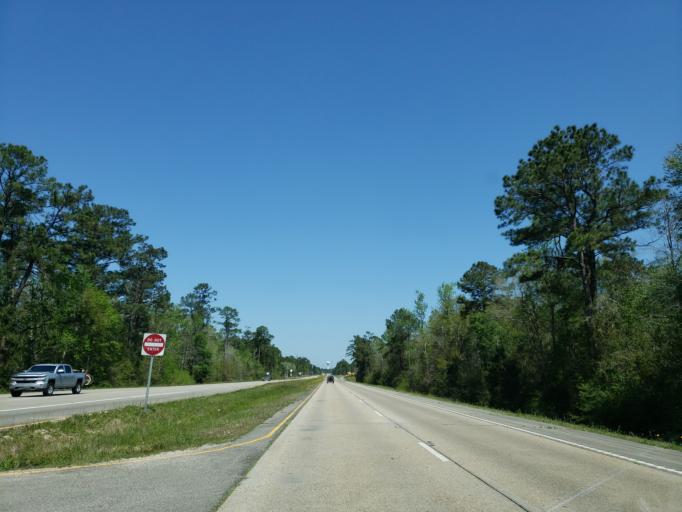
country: US
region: Mississippi
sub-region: Harrison County
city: Lyman
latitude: 30.5638
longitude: -89.1230
